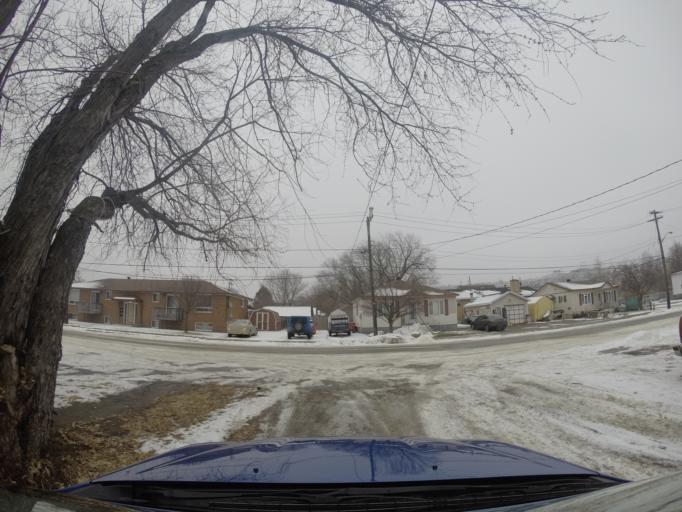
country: CA
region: Ontario
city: Greater Sudbury
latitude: 46.5030
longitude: -80.9846
